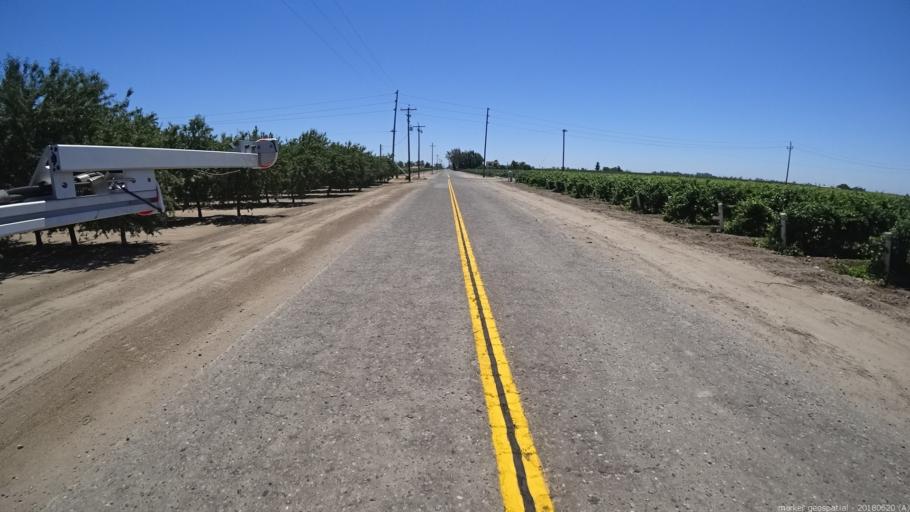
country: US
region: California
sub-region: Madera County
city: Parkwood
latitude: 36.9171
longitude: -120.0373
